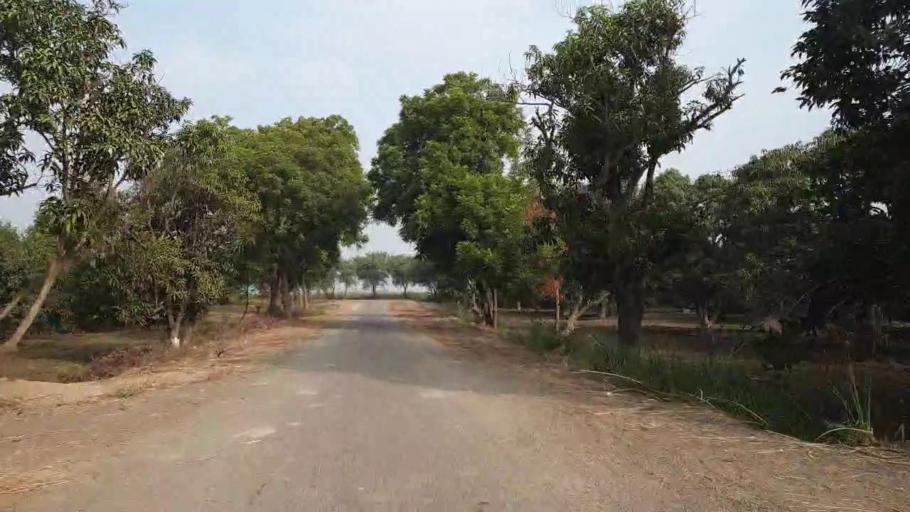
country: PK
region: Sindh
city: Tando Muhammad Khan
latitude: 25.1316
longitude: 68.5865
